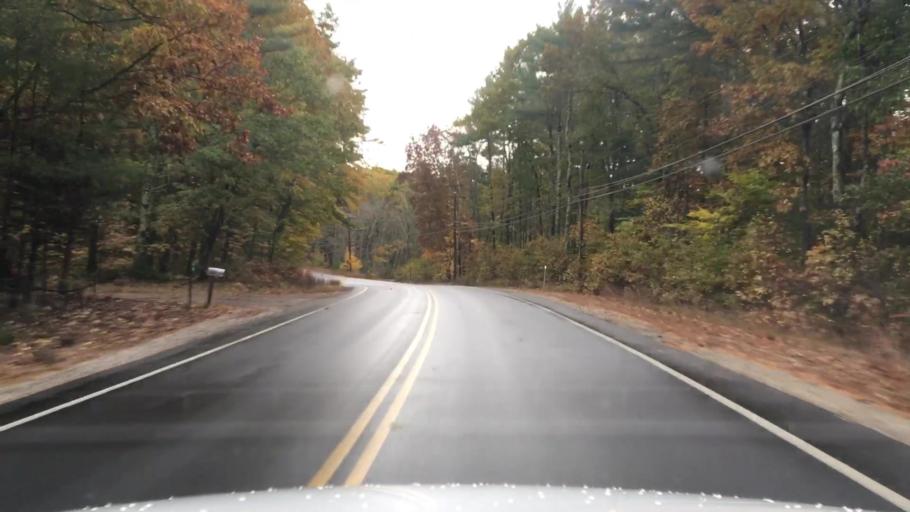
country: US
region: New Hampshire
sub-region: Strafford County
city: Lee
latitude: 43.1253
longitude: -71.0198
